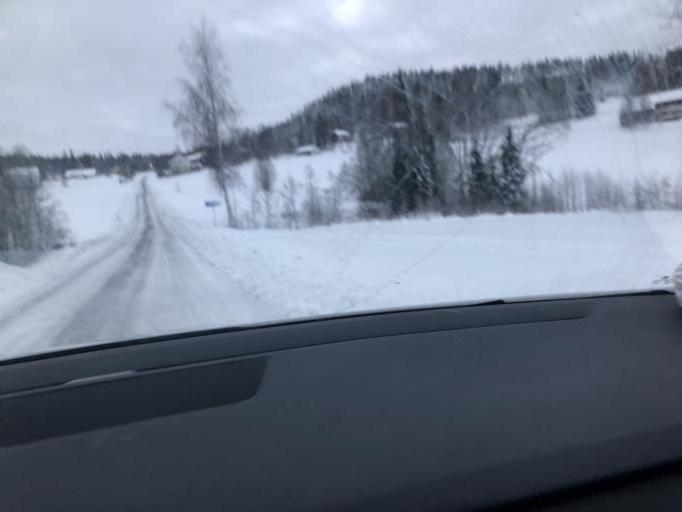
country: SE
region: Vaesternorrland
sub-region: Kramfors Kommun
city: Nordingra
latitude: 62.9118
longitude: 18.2353
